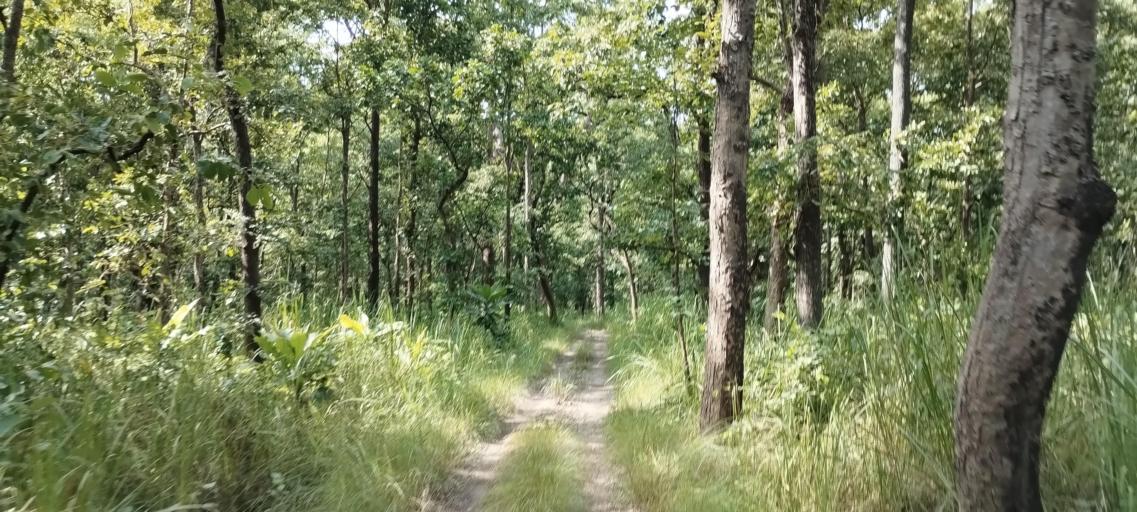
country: NP
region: Far Western
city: Tikapur
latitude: 28.5655
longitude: 81.2931
